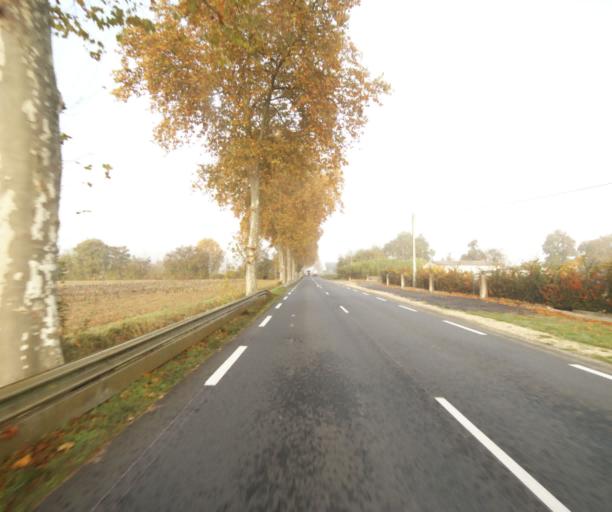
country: FR
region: Midi-Pyrenees
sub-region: Departement du Tarn-et-Garonne
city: Nohic
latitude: 43.9336
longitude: 1.4890
